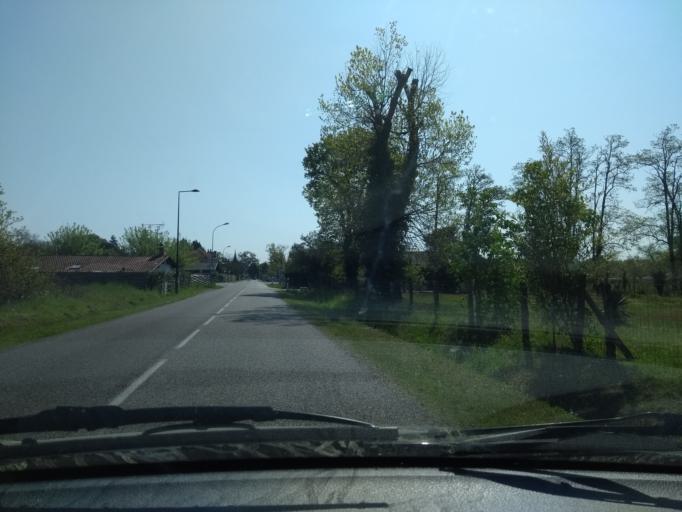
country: FR
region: Aquitaine
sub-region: Departement de la Gironde
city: Belin-Beliet
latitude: 44.5273
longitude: -0.6617
